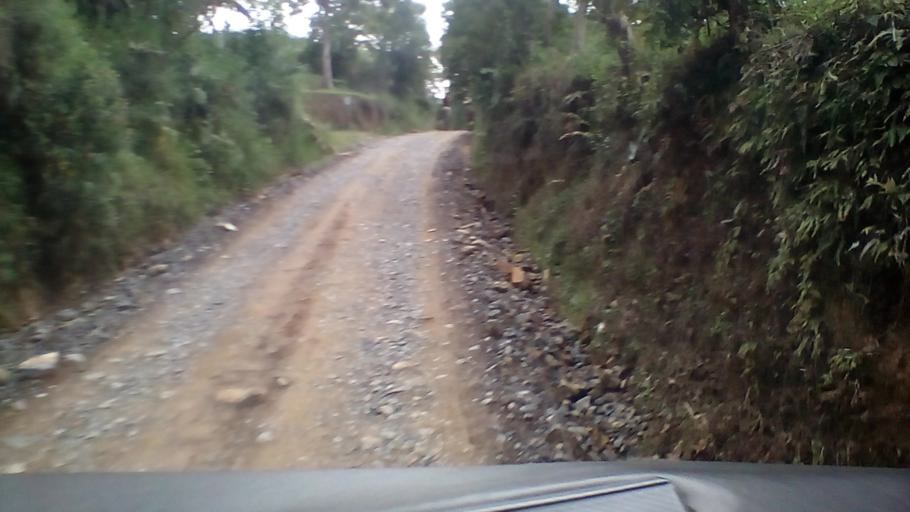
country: CO
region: Boyaca
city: Santana
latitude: 6.0061
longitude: -73.5078
